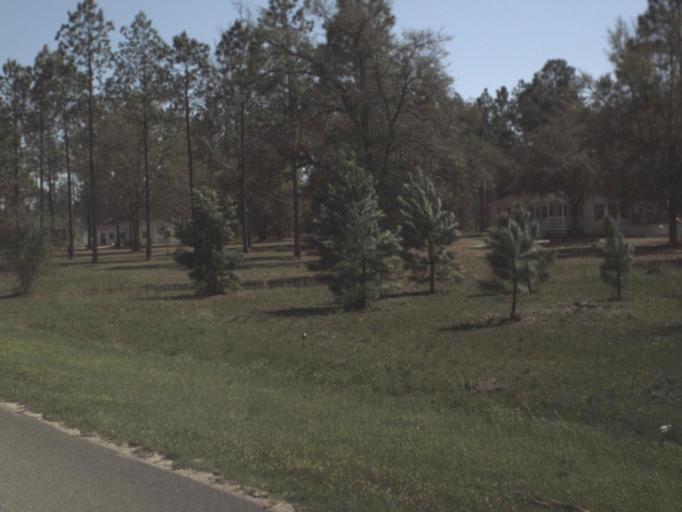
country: US
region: Florida
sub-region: Liberty County
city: Bristol
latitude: 30.4021
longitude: -84.8163
